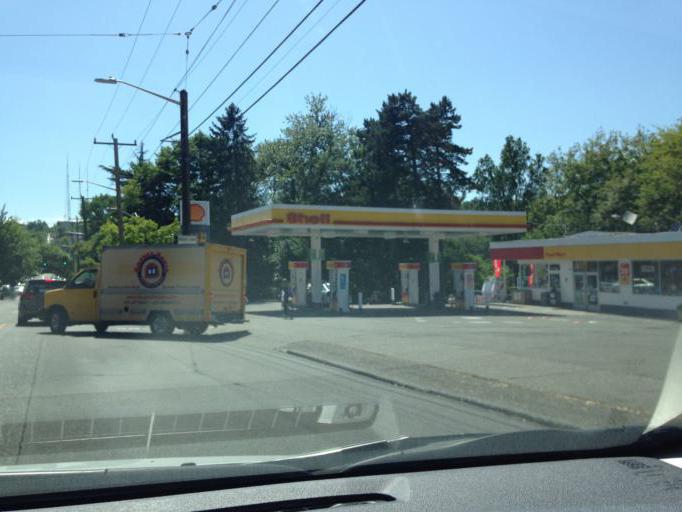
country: US
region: Washington
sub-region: King County
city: Seattle
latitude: 47.6266
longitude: -122.2916
